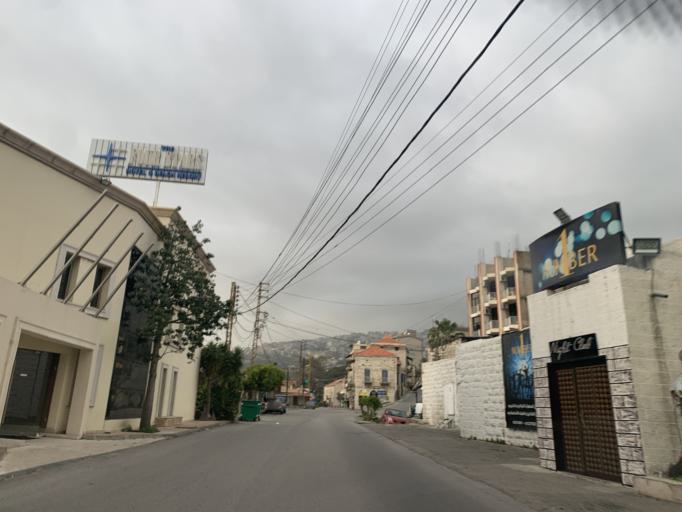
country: LB
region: Mont-Liban
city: Djounie
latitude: 34.0051
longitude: 35.6451
